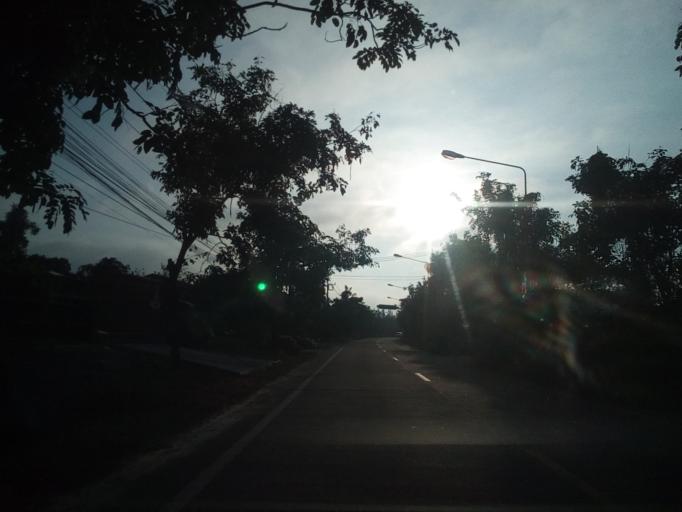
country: TH
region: Lamphun
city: Ban Thi
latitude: 18.6303
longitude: 99.0624
